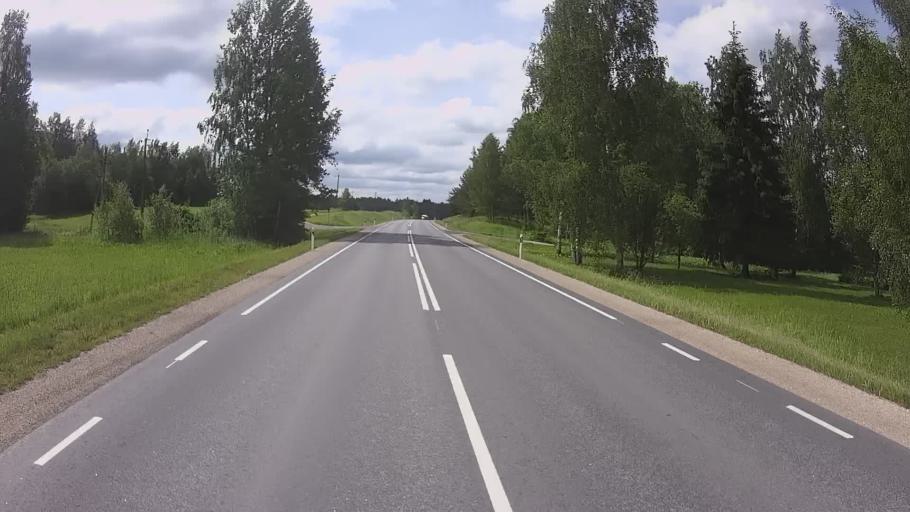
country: EE
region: Polvamaa
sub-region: Polva linn
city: Polva
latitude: 58.0507
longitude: 27.0765
